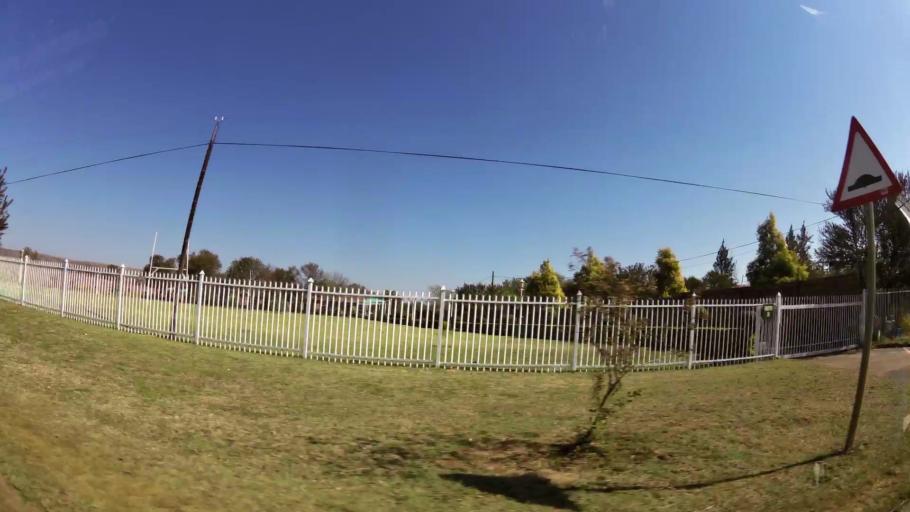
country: ZA
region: Gauteng
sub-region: City of Tshwane Metropolitan Municipality
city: Pretoria
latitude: -25.6583
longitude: 28.2641
